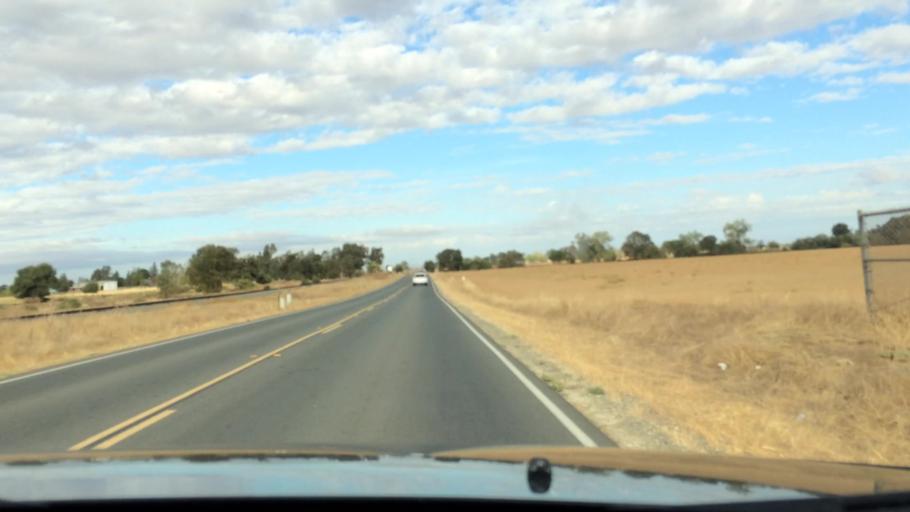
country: US
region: California
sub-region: Sacramento County
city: Herald
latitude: 38.2974
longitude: -121.2412
